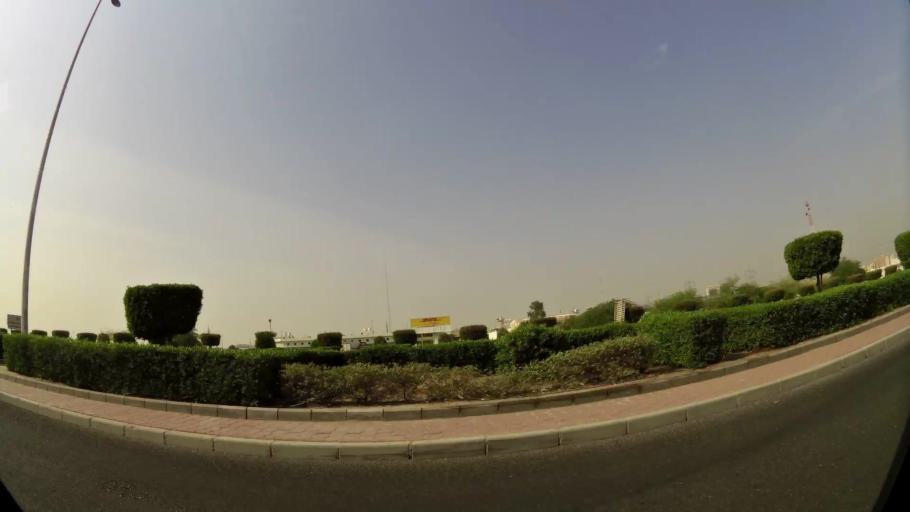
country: KW
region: Al Asimah
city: Ar Rabiyah
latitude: 29.2966
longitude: 47.9280
